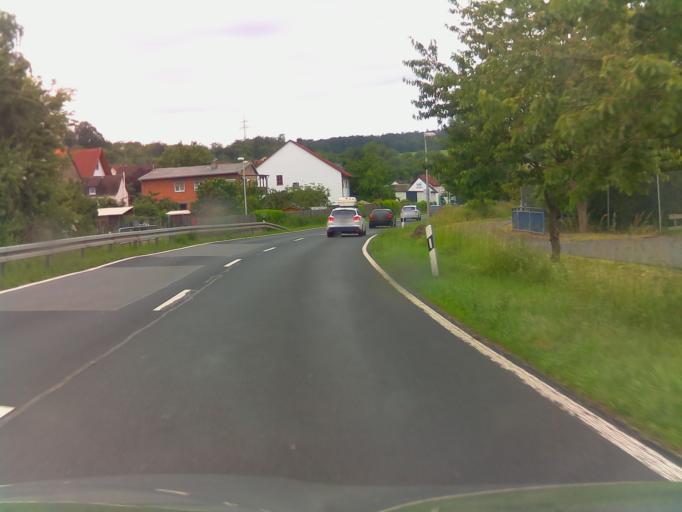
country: DE
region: Bavaria
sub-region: Regierungsbezirk Unterfranken
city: Eschau
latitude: 49.8193
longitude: 9.2525
